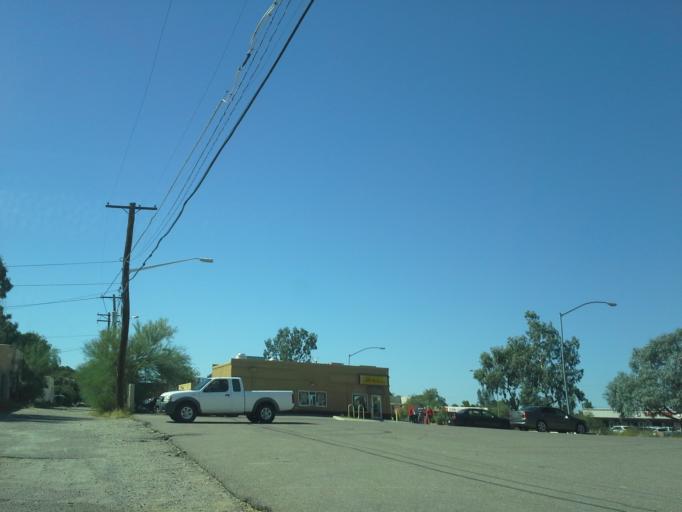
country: US
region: Arizona
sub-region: Pima County
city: Tucson
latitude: 32.2356
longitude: -110.9283
